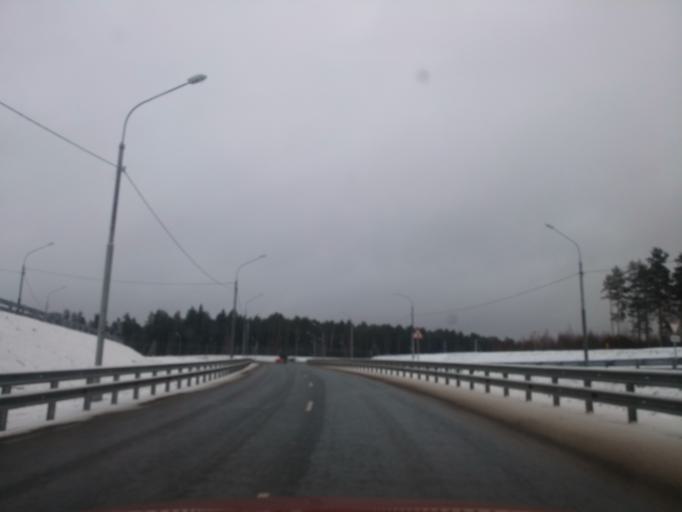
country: RU
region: Tverskaya
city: Likhoslavl'
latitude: 56.9441
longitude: 35.4979
